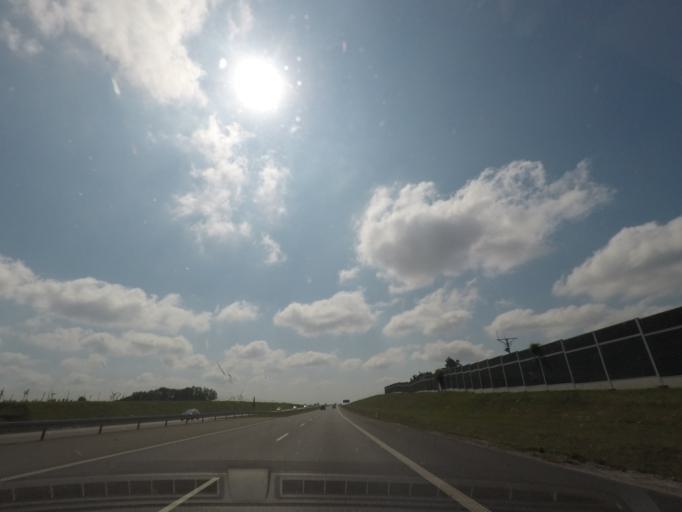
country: PL
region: Kujawsko-Pomorskie
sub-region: Powiat wloclawski
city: Brzesc Kujawski
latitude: 52.6474
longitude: 18.9413
